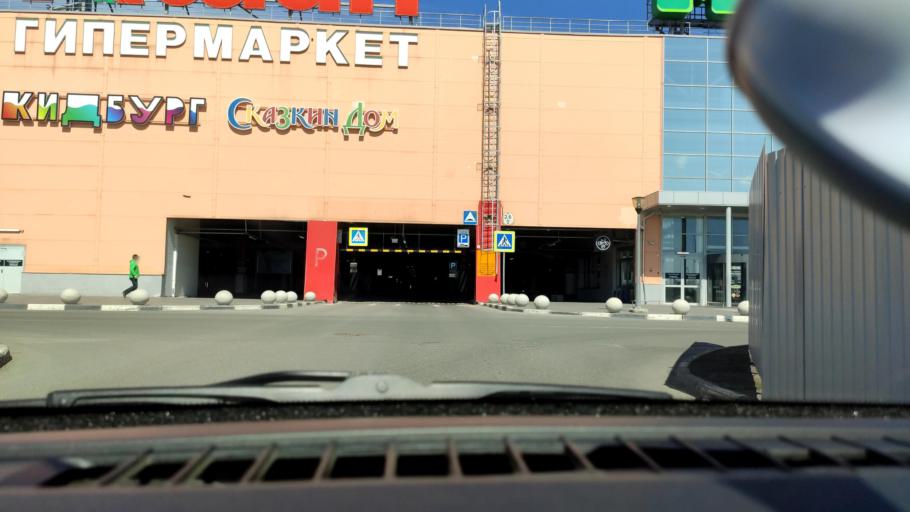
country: RU
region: Samara
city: Novosemeykino
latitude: 53.3257
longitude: 50.3051
